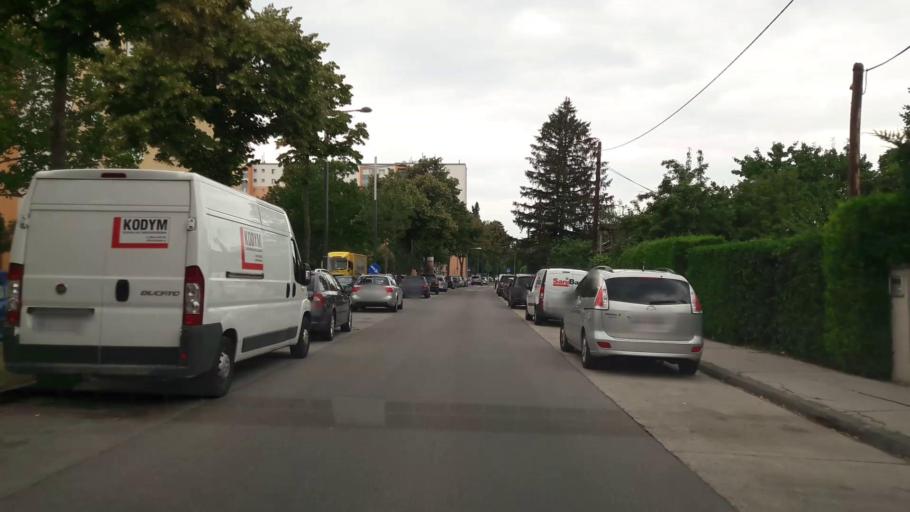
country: AT
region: Lower Austria
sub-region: Politischer Bezirk Wien-Umgebung
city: Schwechat
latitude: 48.1707
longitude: 16.4312
